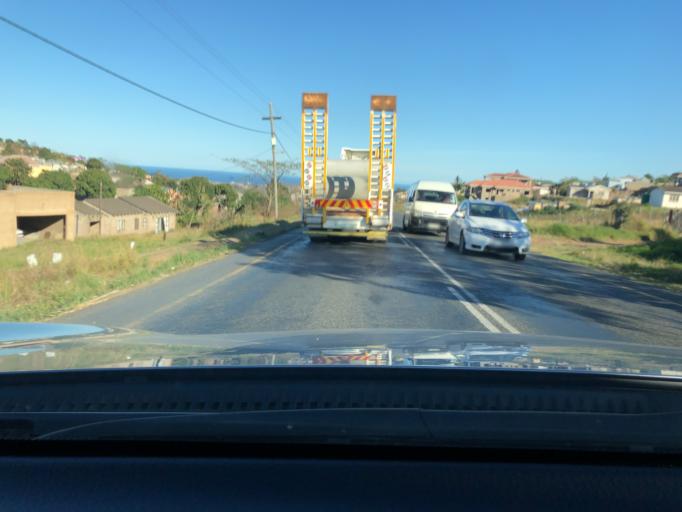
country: ZA
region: KwaZulu-Natal
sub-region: eThekwini Metropolitan Municipality
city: Umkomaas
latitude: -30.0109
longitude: 30.8052
